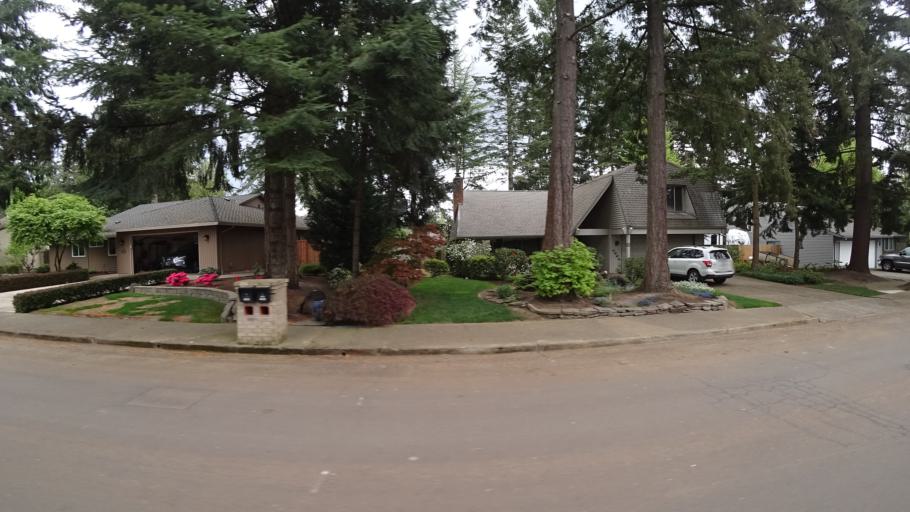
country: US
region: Oregon
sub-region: Washington County
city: Rockcreek
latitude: 45.5538
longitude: -122.8858
